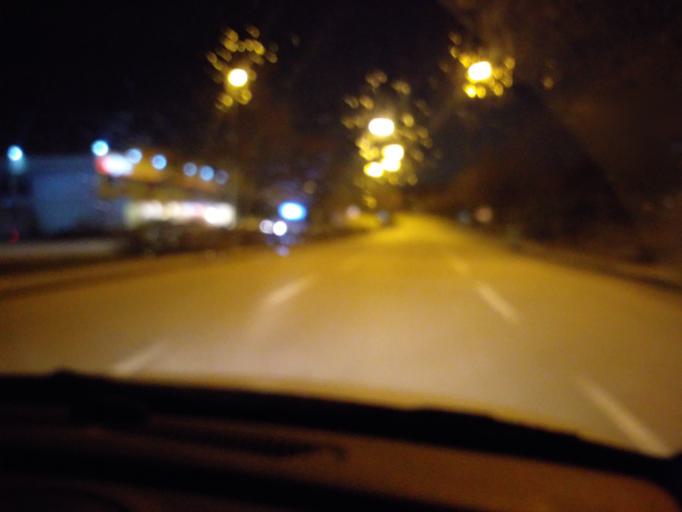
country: TR
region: Ankara
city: Batikent
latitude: 39.8867
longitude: 32.7175
